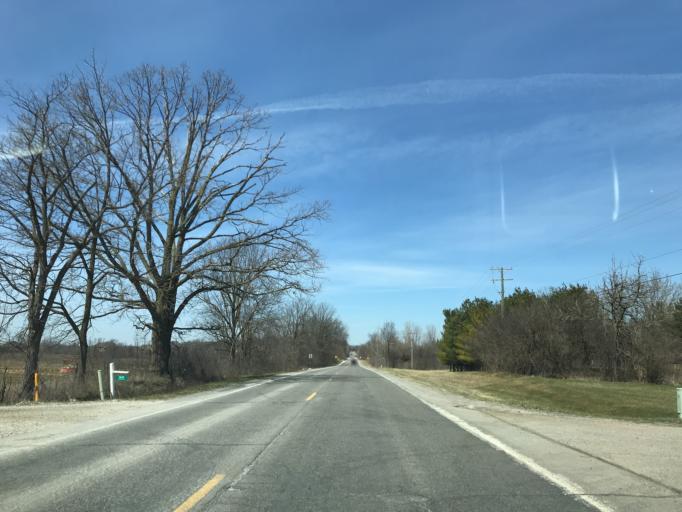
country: US
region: Michigan
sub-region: Washtenaw County
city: Ann Arbor
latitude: 42.3283
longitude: -83.7080
